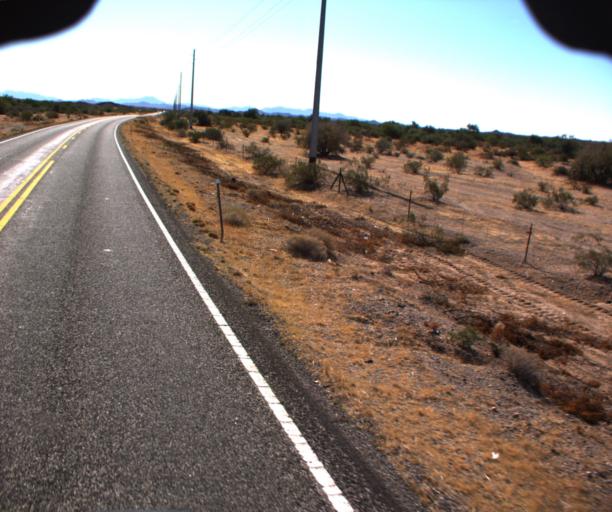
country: US
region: Arizona
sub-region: La Paz County
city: Cienega Springs
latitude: 33.9939
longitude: -114.0950
